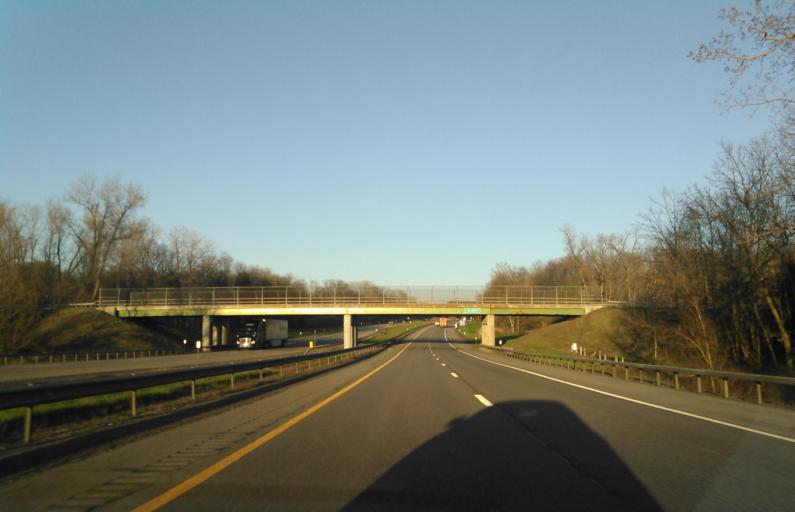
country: US
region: New York
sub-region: Ontario County
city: Victor
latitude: 43.0142
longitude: -77.4660
